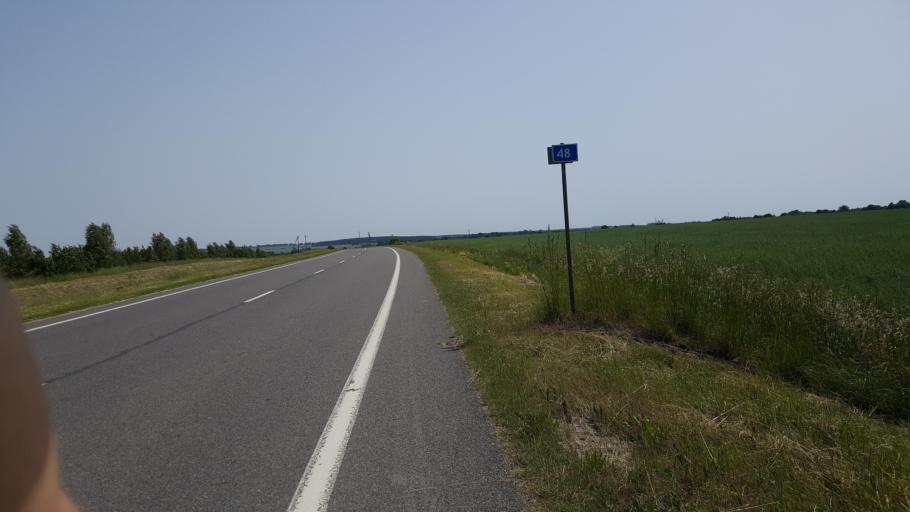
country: BY
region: Brest
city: Kamyanyets
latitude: 52.4363
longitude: 23.8317
